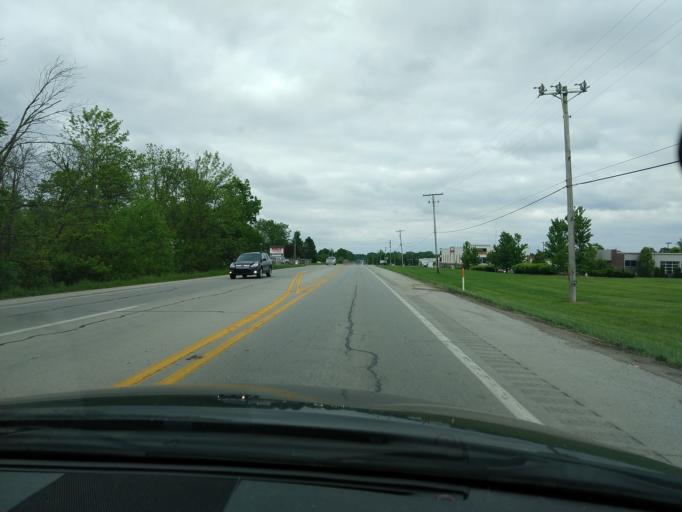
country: US
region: Indiana
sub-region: Hamilton County
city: Noblesville
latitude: 40.0433
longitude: -86.0594
